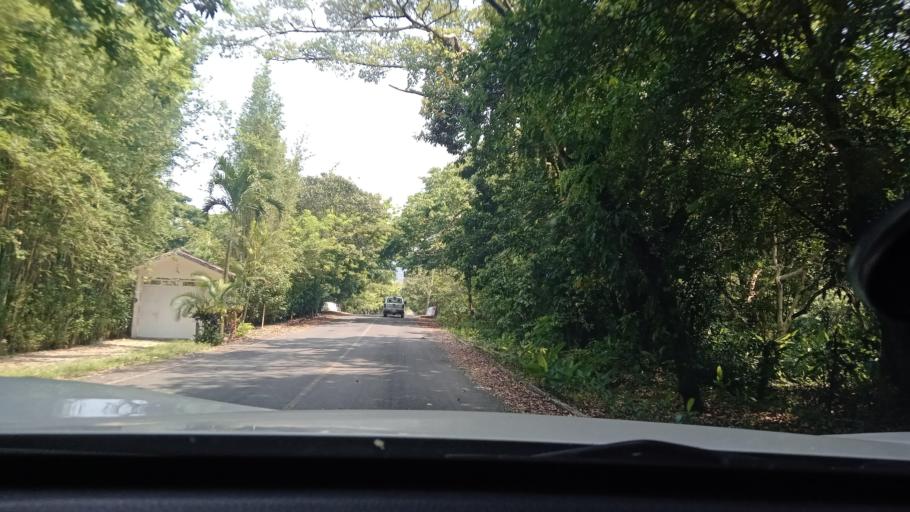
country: MX
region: Veracruz
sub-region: San Andres Tuxtla
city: Santa Rosa Abata
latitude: 18.5627
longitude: -95.0593
